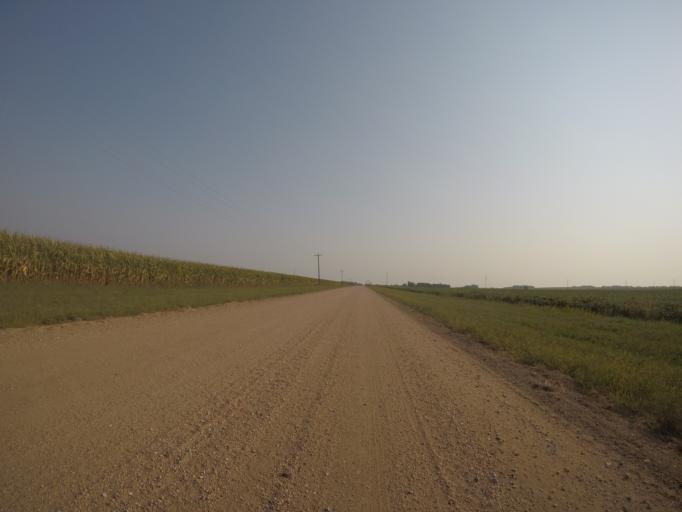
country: US
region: Nebraska
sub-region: Gage County
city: Beatrice
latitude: 40.2801
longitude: -96.8223
